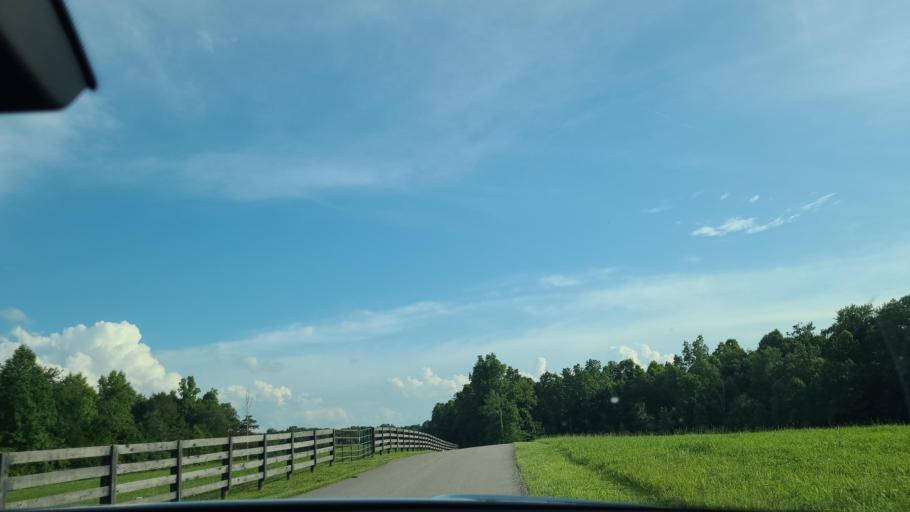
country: US
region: Kentucky
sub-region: Whitley County
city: Corbin
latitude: 36.8907
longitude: -84.2340
